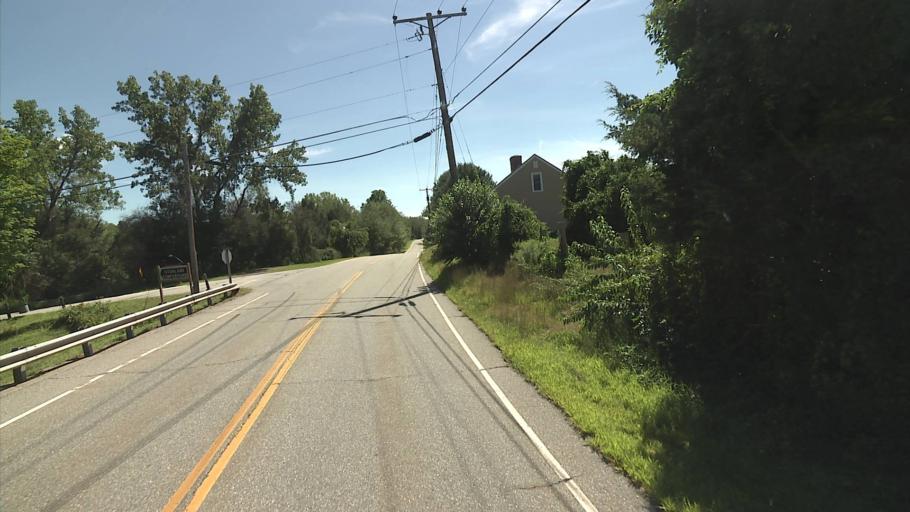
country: US
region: Connecticut
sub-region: New London County
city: Baltic
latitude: 41.6778
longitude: -72.0841
